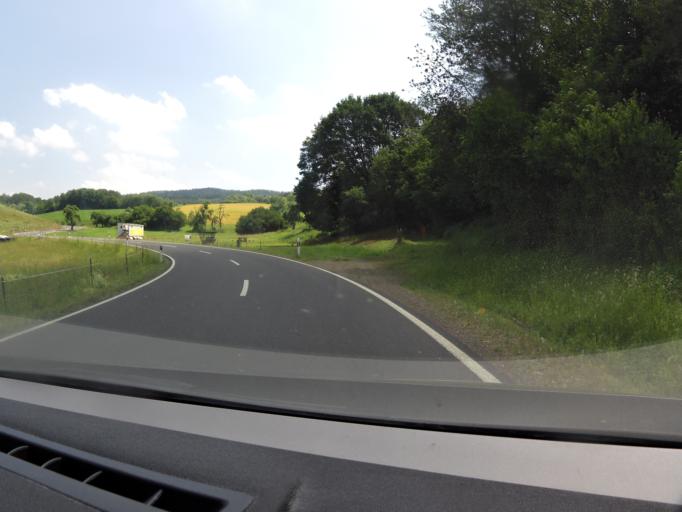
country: DE
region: Hesse
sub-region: Regierungsbezirk Kassel
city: Ronshausen
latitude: 50.9814
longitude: 9.8862
